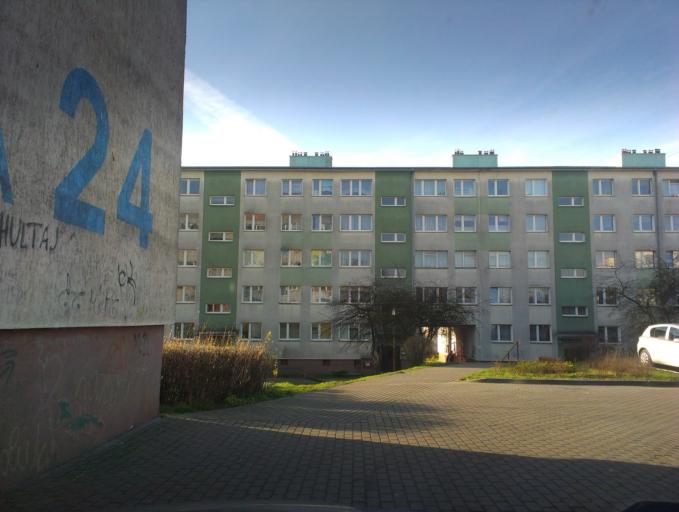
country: PL
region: West Pomeranian Voivodeship
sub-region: Powiat szczecinecki
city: Szczecinek
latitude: 53.7010
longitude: 16.7031
